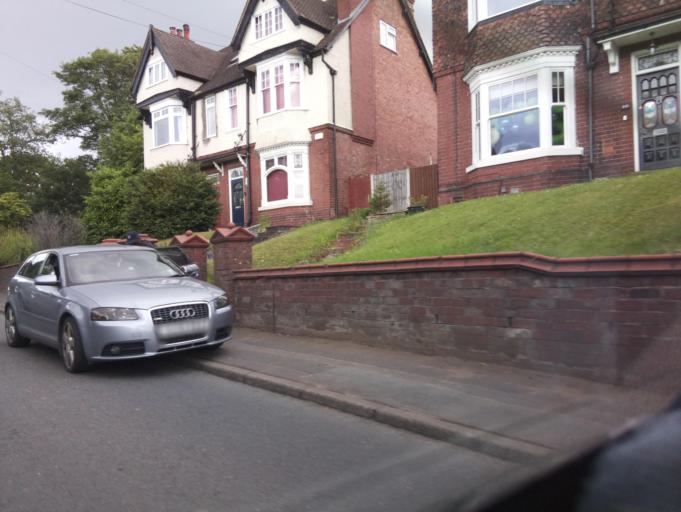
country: GB
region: England
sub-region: Worcestershire
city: Kidderminster
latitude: 52.3823
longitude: -2.2370
